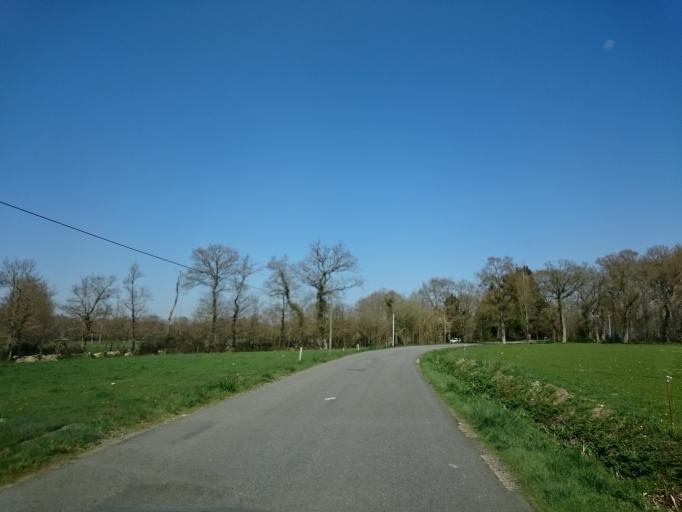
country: FR
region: Brittany
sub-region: Departement d'Ille-et-Vilaine
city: Orgeres
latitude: 47.9930
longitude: -1.6848
